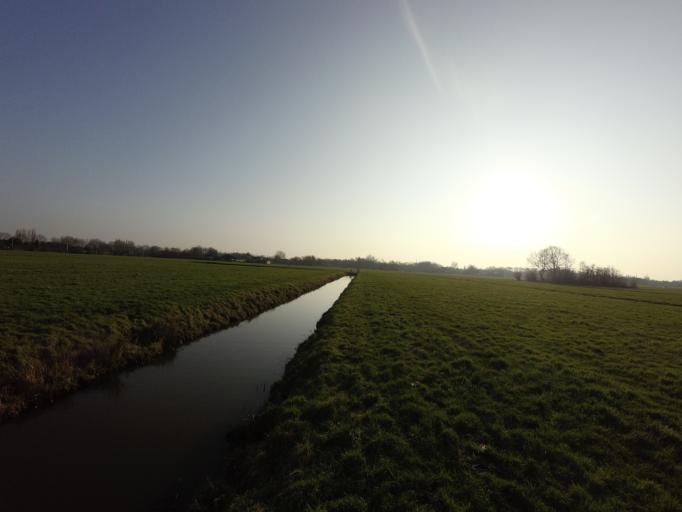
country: NL
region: Utrecht
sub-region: Gemeente Woerden
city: Woerden
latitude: 52.0997
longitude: 4.8914
